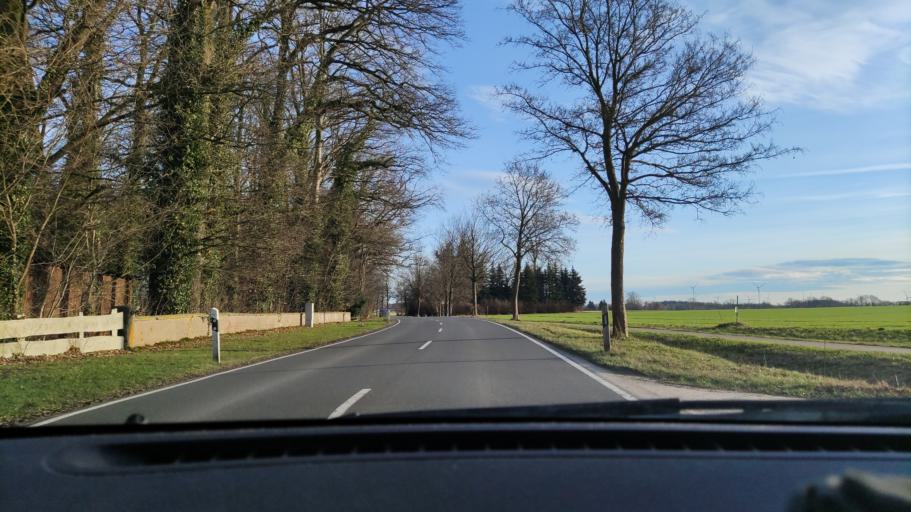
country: DE
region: Lower Saxony
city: Ebstorf
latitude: 53.0359
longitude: 10.3966
